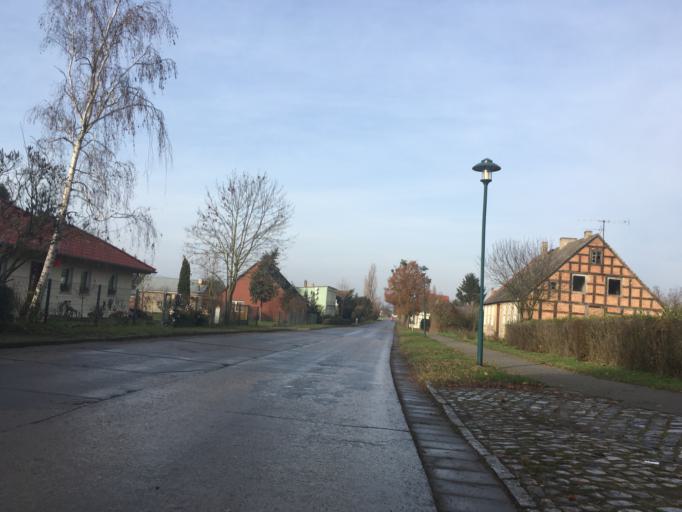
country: DE
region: Brandenburg
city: Wriezen
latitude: 52.7656
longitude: 14.1629
